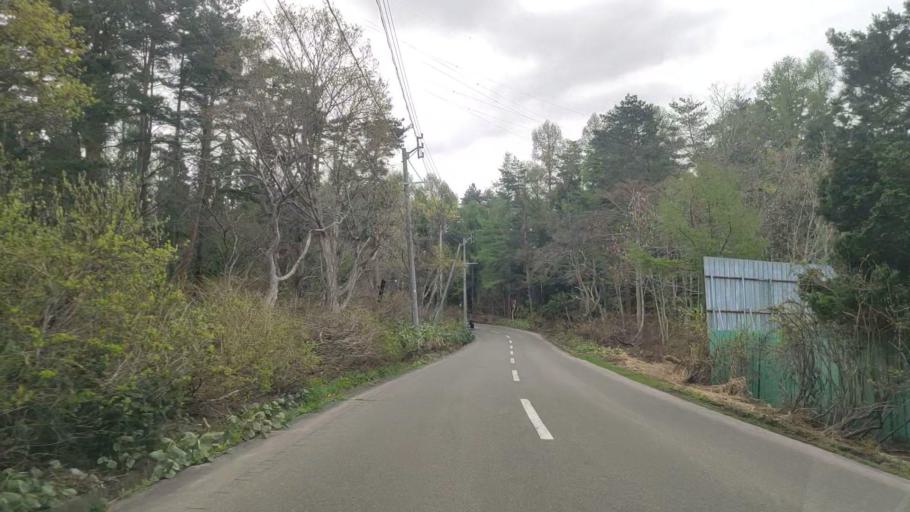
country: JP
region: Aomori
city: Aomori Shi
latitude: 40.7476
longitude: 140.8210
